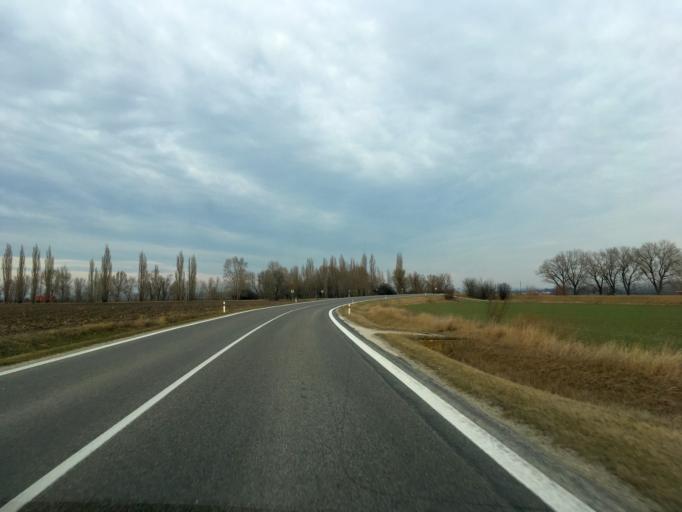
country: SK
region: Nitriansky
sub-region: Okres Nove Zamky
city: Nove Zamky
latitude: 47.9956
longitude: 18.2410
